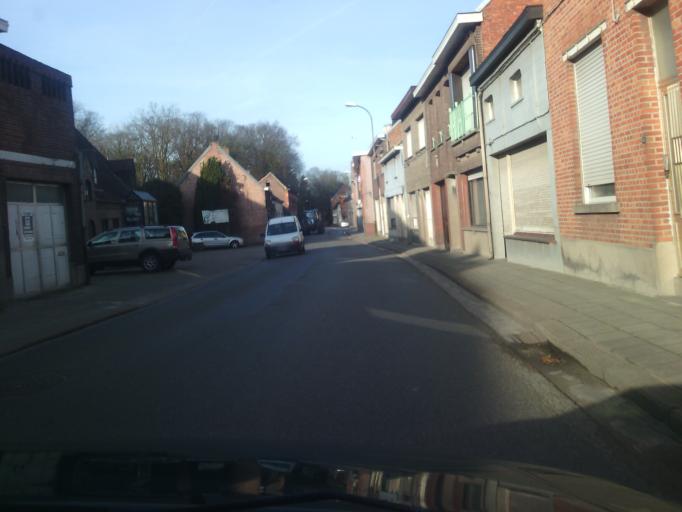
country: BE
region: Flanders
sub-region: Provincie Oost-Vlaanderen
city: Berlare
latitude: 51.0213
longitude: 4.0059
